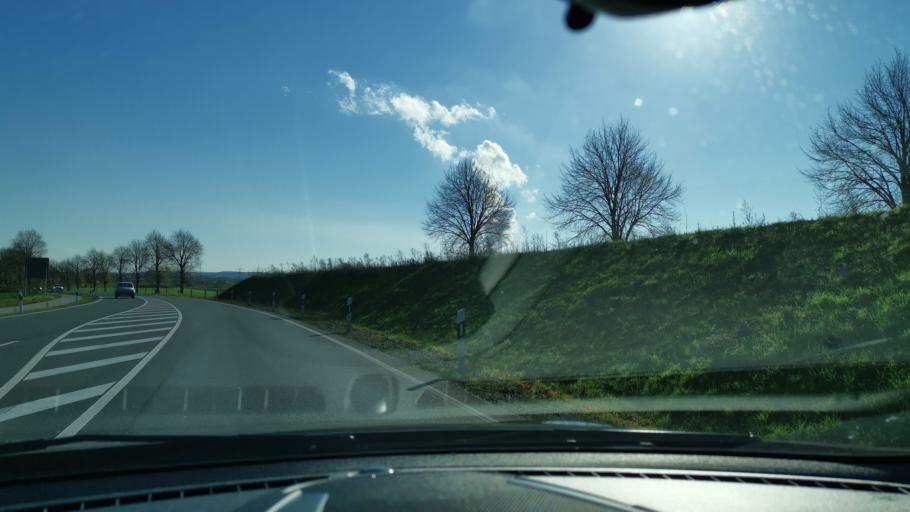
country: DE
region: North Rhine-Westphalia
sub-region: Regierungsbezirk Dusseldorf
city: Rommerskirchen
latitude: 51.0428
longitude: 6.6679
